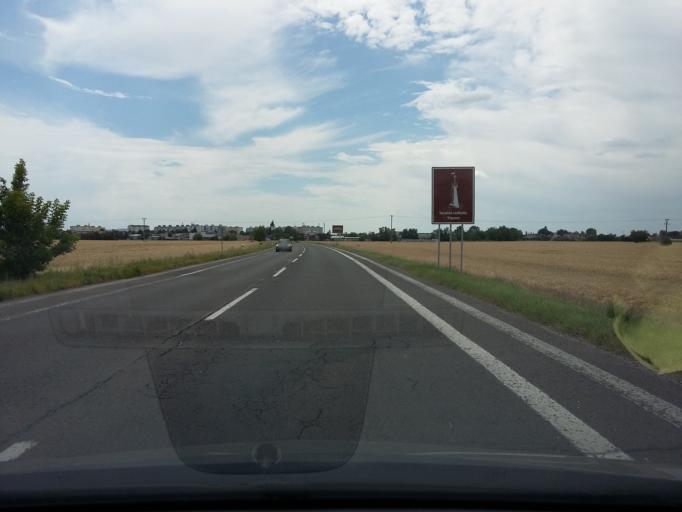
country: SK
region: Bratislavsky
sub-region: Okres Malacky
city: Malacky
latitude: 48.4513
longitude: 17.0105
